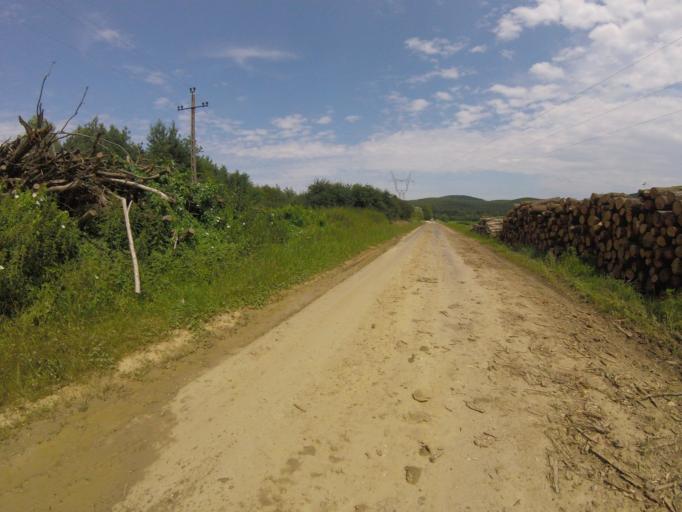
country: HR
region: Medimurska
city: Podturen
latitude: 46.5435
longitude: 16.6043
